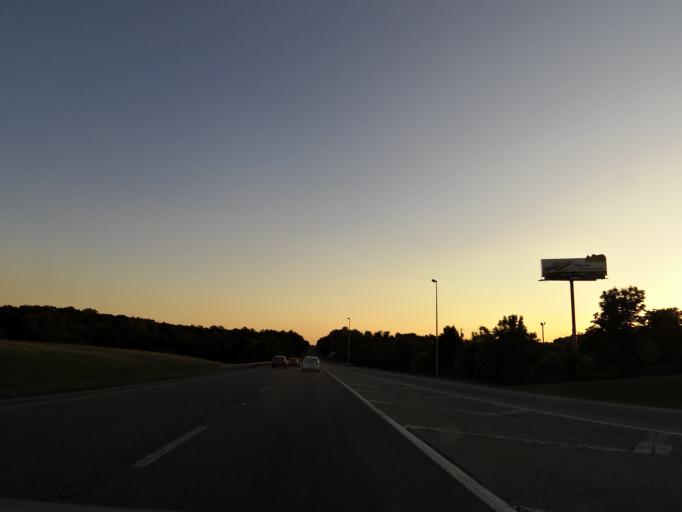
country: US
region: Tennessee
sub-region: Greene County
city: Mosheim
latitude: 36.2230
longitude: -83.0450
